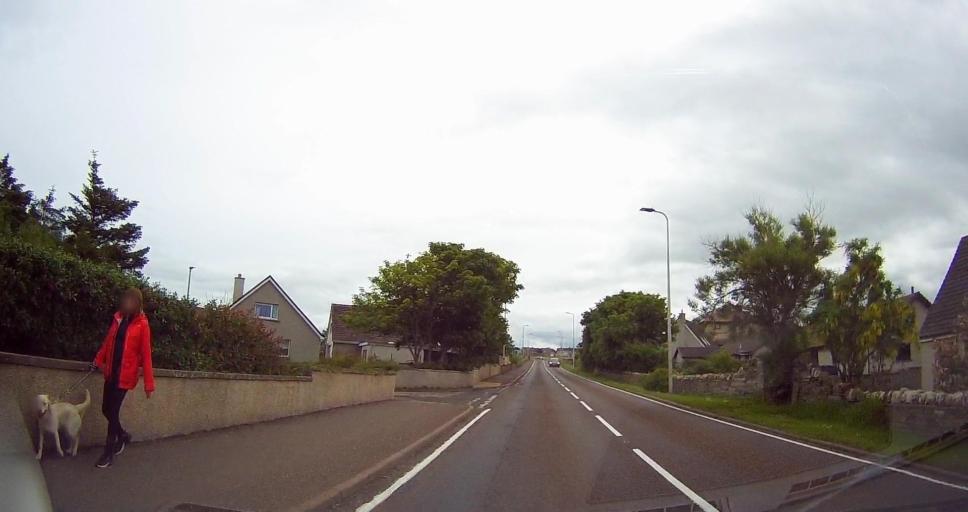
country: GB
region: Scotland
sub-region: Highland
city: Thurso
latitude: 58.6005
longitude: -3.5399
